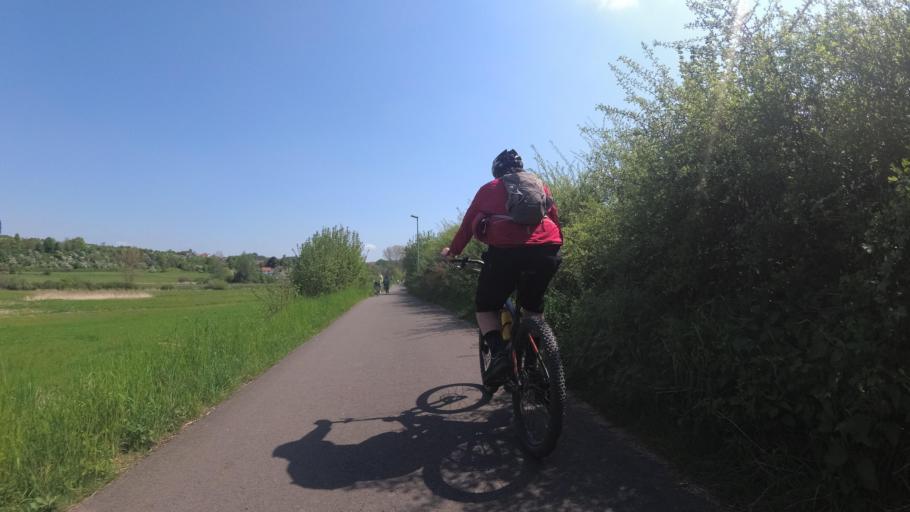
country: DE
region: Rheinland-Pfalz
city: Niedermohr
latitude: 49.4555
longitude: 7.4971
